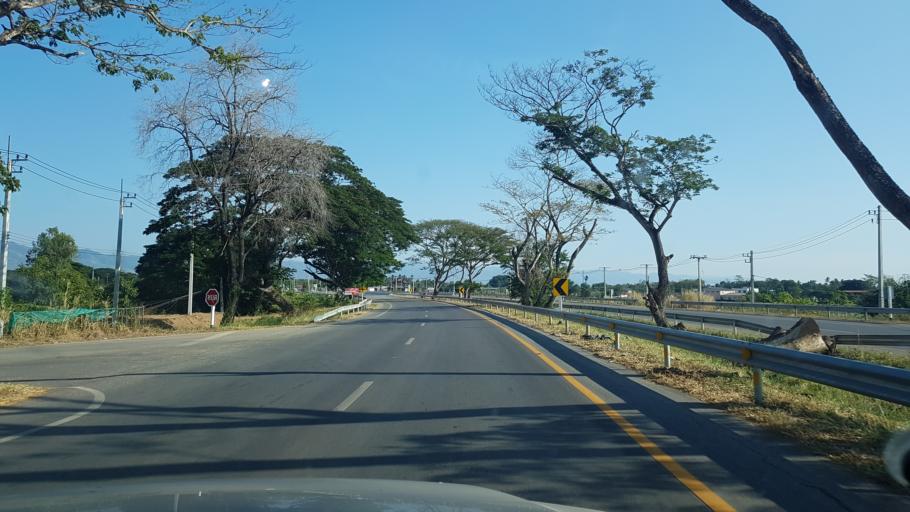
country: TH
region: Phetchabun
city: Lom Sak
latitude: 16.7288
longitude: 101.2391
